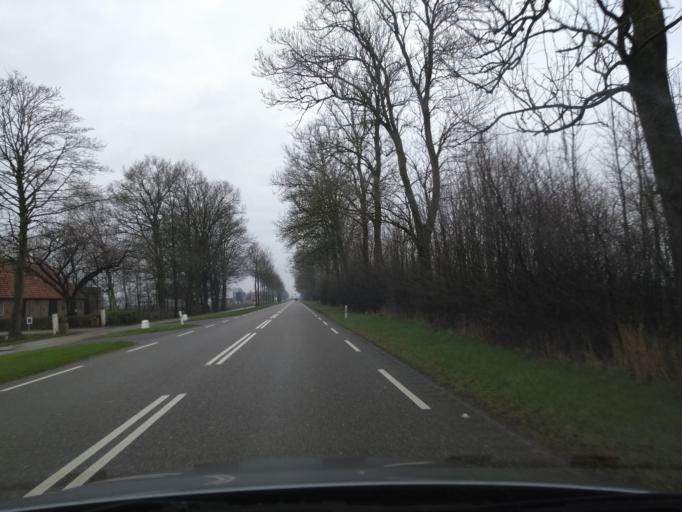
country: NL
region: Overijssel
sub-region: Gemeente Steenwijkerland
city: Vollenhove
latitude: 52.7073
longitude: 5.8837
